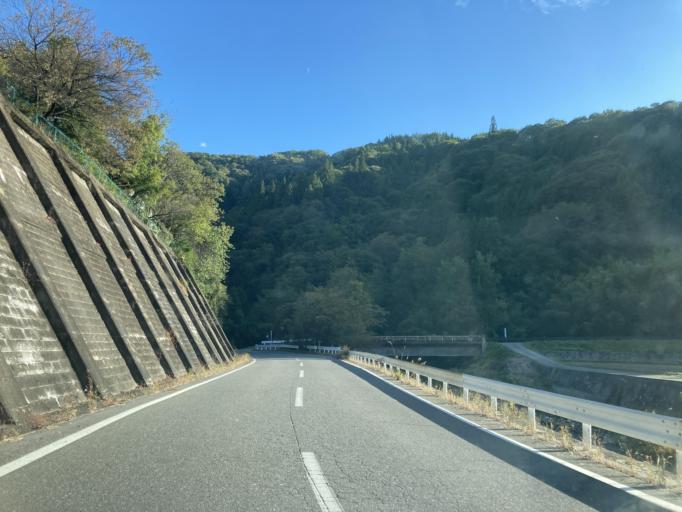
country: JP
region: Nagano
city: Omachi
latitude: 36.4715
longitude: 137.9384
